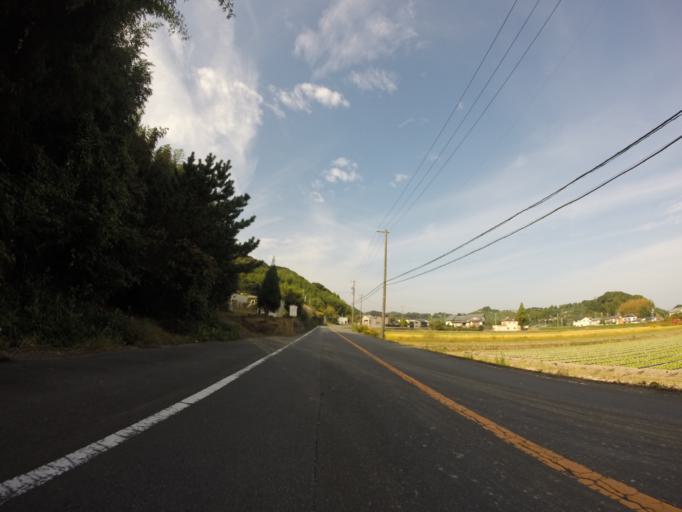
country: JP
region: Shizuoka
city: Shimada
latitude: 34.7521
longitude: 138.1996
